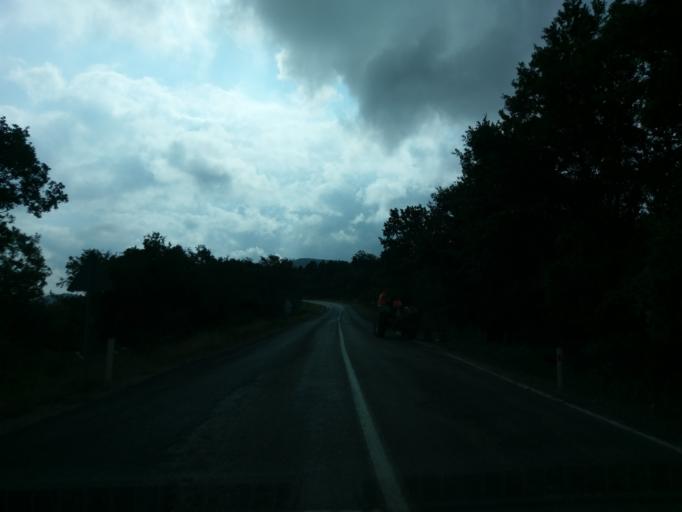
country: TR
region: Sinop
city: Ayancik
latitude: 41.9443
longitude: 34.6964
